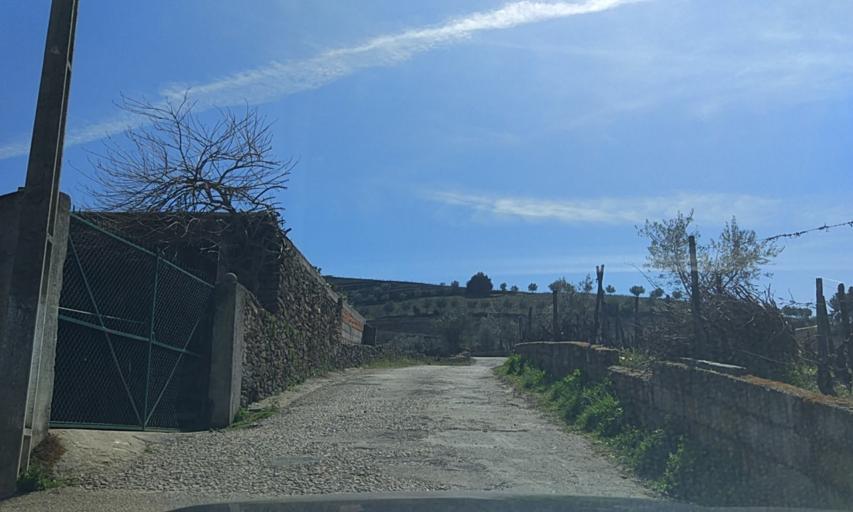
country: PT
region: Vila Real
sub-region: Sabrosa
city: Sabrosa
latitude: 41.3064
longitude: -7.5465
